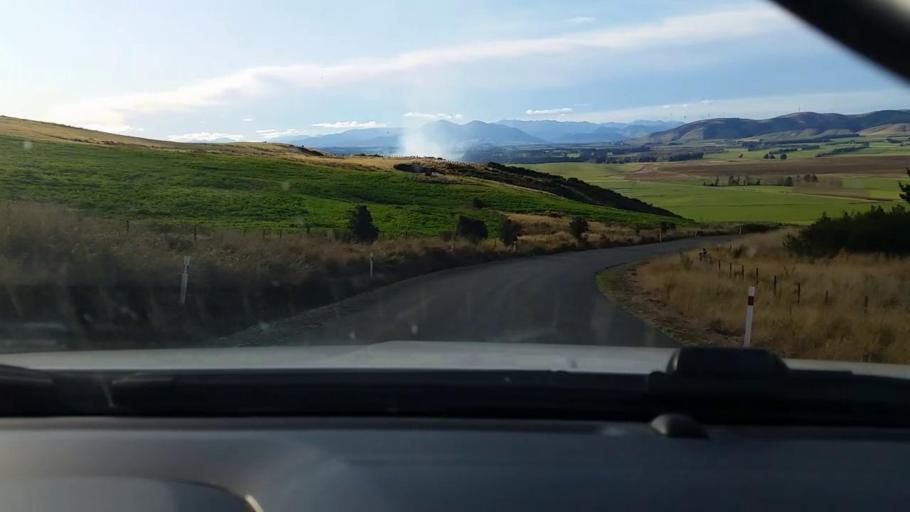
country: NZ
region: Southland
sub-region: Southland District
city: Winton
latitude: -45.8197
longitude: 168.1739
